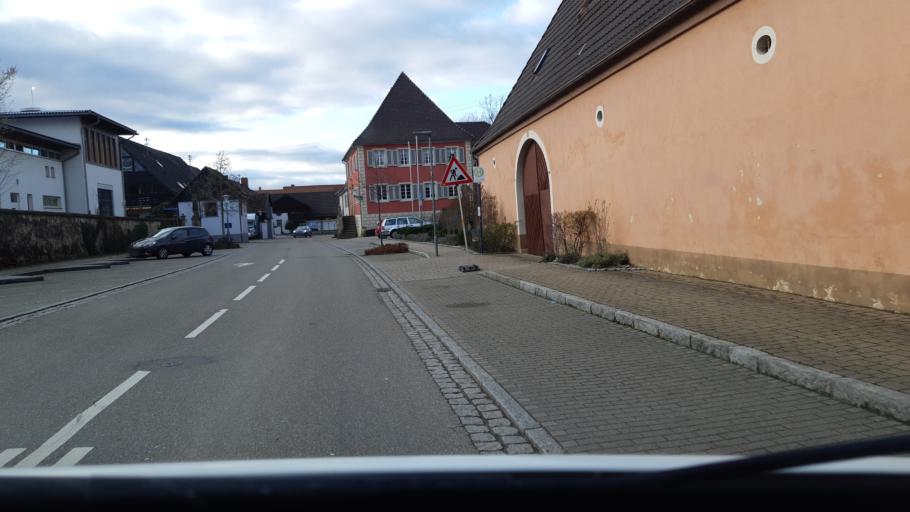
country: DE
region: Baden-Wuerttemberg
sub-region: Freiburg Region
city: Eschbach
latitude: 47.9034
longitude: 7.6647
